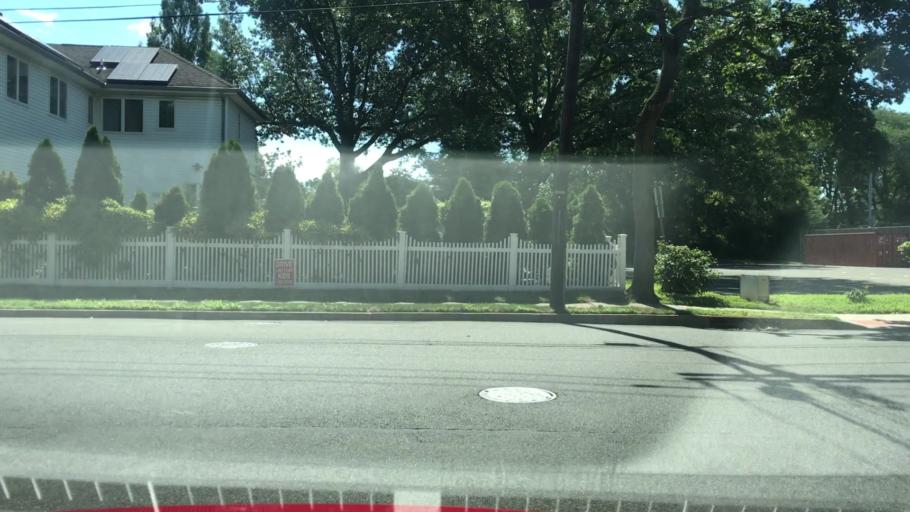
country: US
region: New Jersey
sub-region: Bergen County
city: Leonia
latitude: 40.8794
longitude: -73.9993
